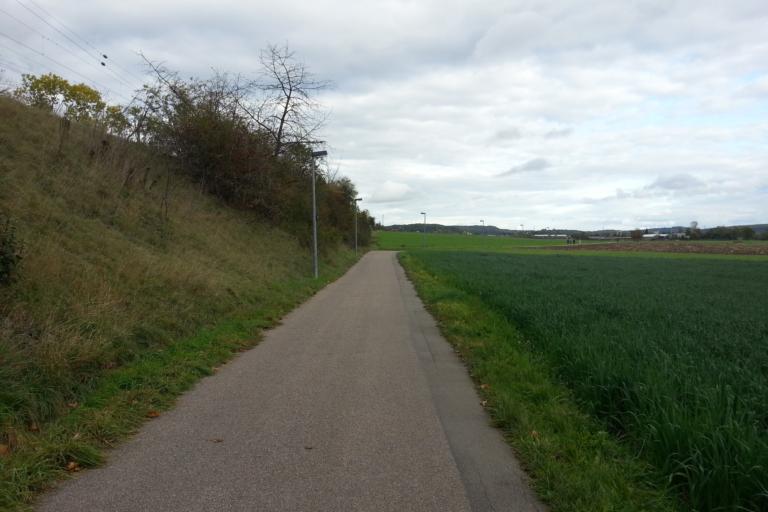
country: DE
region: Baden-Wuerttemberg
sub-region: Regierungsbezirk Stuttgart
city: Renningen
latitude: 48.7721
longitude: 8.9087
